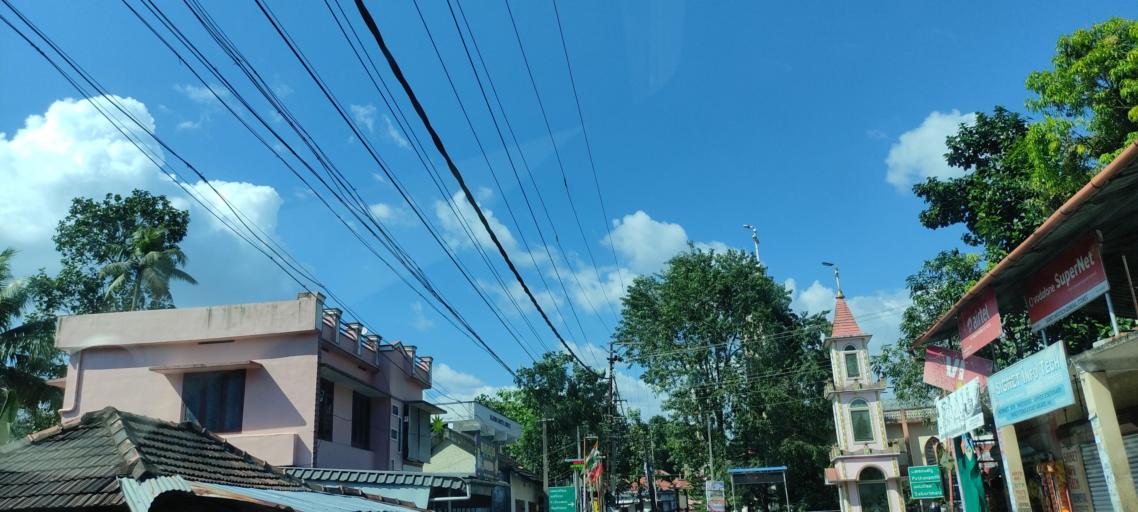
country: IN
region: Kerala
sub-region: Pattanamtitta
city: Adur
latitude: 9.1749
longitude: 76.7413
